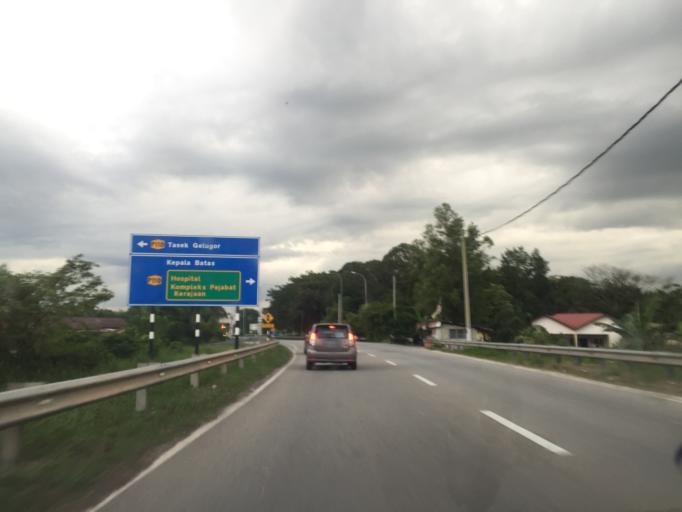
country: MY
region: Penang
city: Tasek Glugor
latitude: 5.5560
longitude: 100.5005
